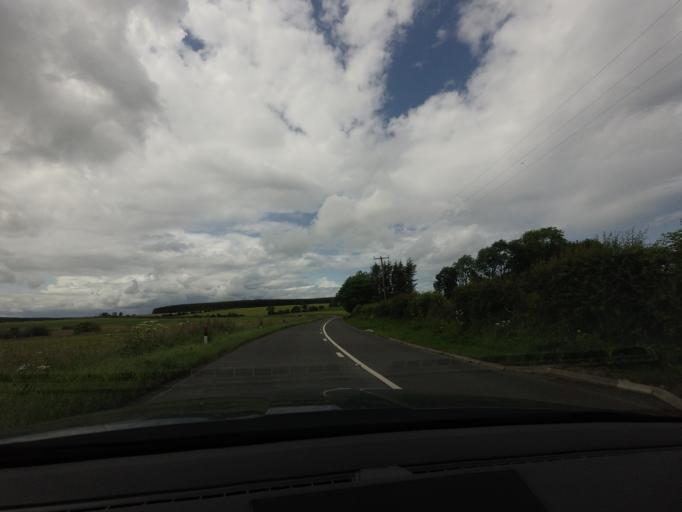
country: GB
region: Scotland
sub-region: Aberdeenshire
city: Whitehills
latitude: 57.6528
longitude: -2.6206
